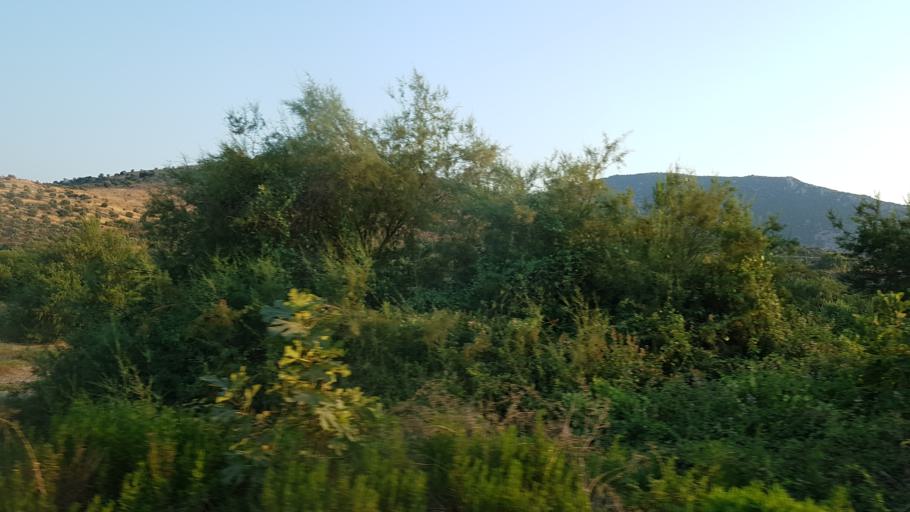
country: TR
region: Izmir
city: Selcuk
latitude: 37.9502
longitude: 27.3492
